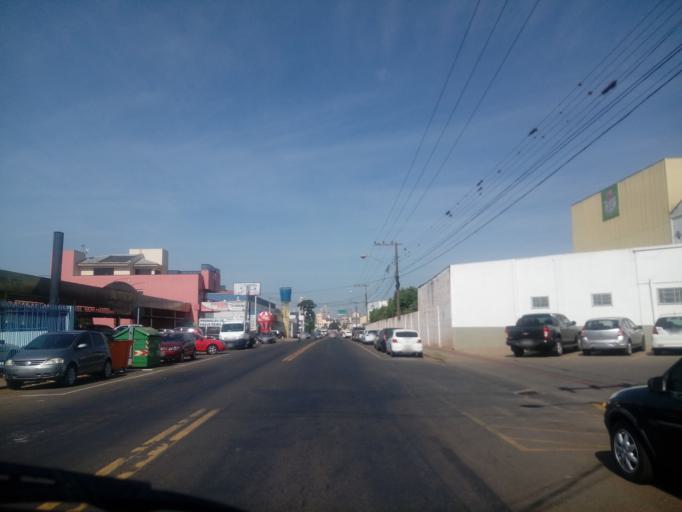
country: BR
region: Santa Catarina
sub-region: Chapeco
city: Chapeco
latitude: -27.0893
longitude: -52.6222
